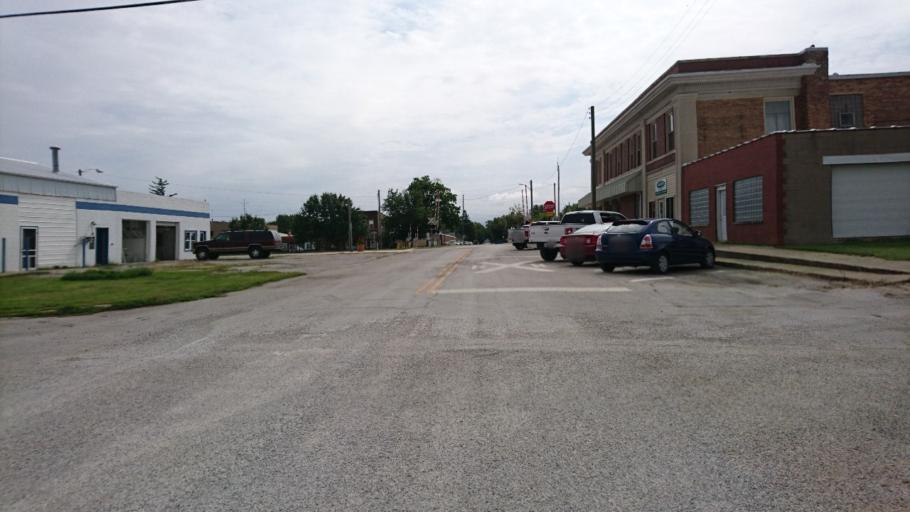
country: US
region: Illinois
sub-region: Livingston County
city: Odell
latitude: 41.0030
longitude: -88.5265
